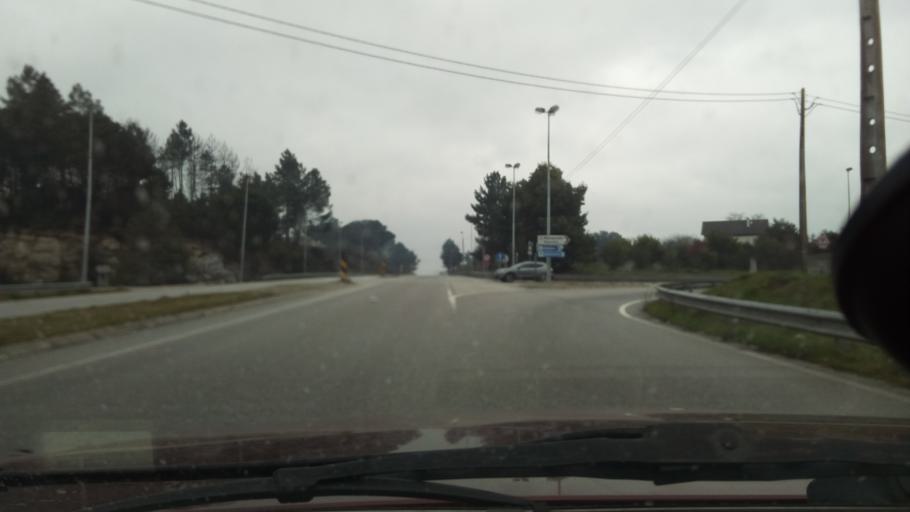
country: PT
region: Viseu
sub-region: Mangualde
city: Mangualde
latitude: 40.6048
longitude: -7.7834
